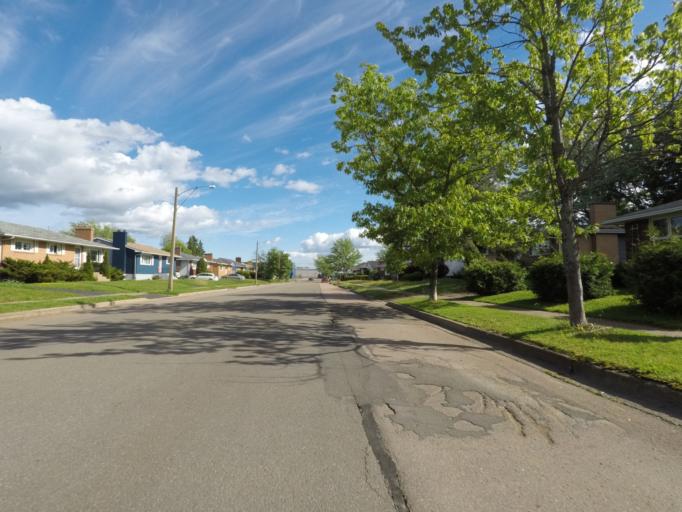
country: CA
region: New Brunswick
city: Moncton
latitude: 46.0966
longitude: -64.8270
